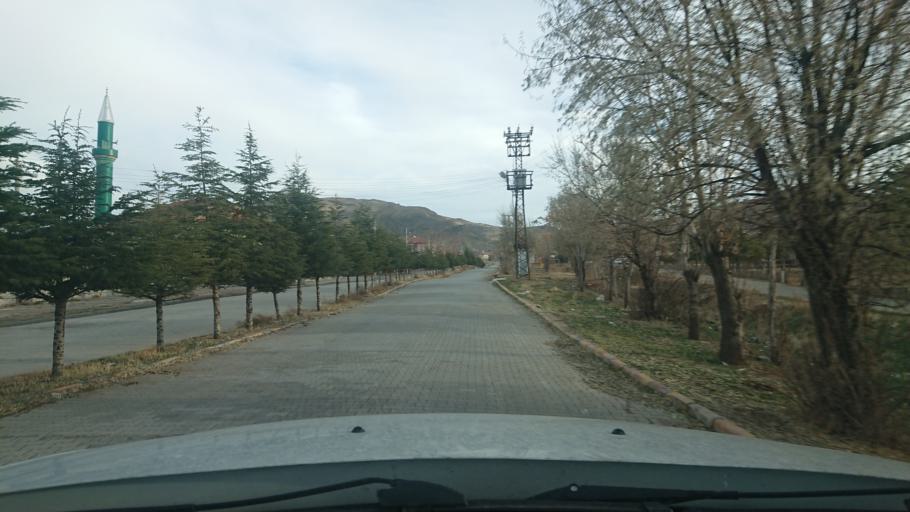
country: TR
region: Aksaray
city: Acipinar
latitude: 38.6121
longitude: 33.7792
